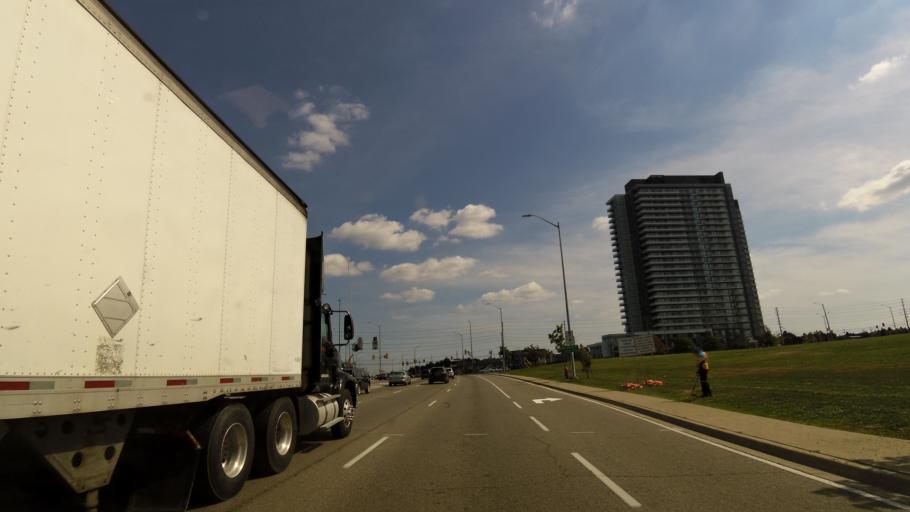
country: CA
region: Ontario
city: Mississauga
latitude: 43.5597
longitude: -79.7083
